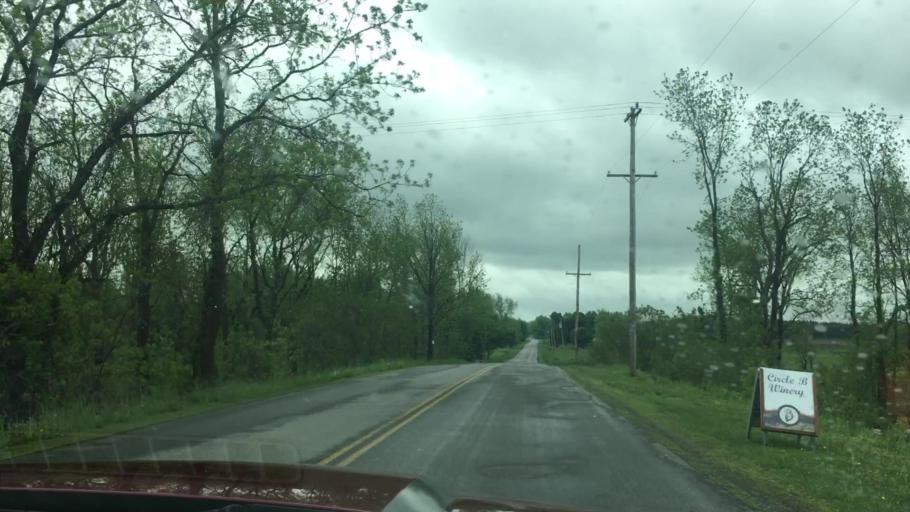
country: US
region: New York
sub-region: Genesee County
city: Batavia
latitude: 43.0799
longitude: -78.1395
